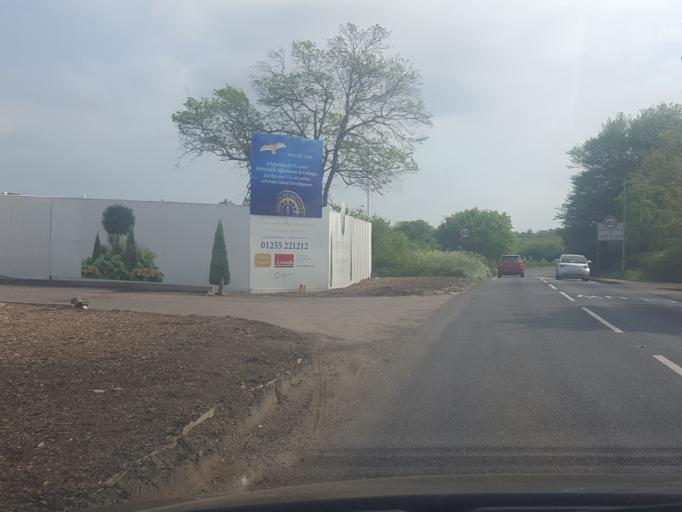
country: GB
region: England
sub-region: Essex
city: Frinton-on-Sea
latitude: 51.8400
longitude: 1.2183
